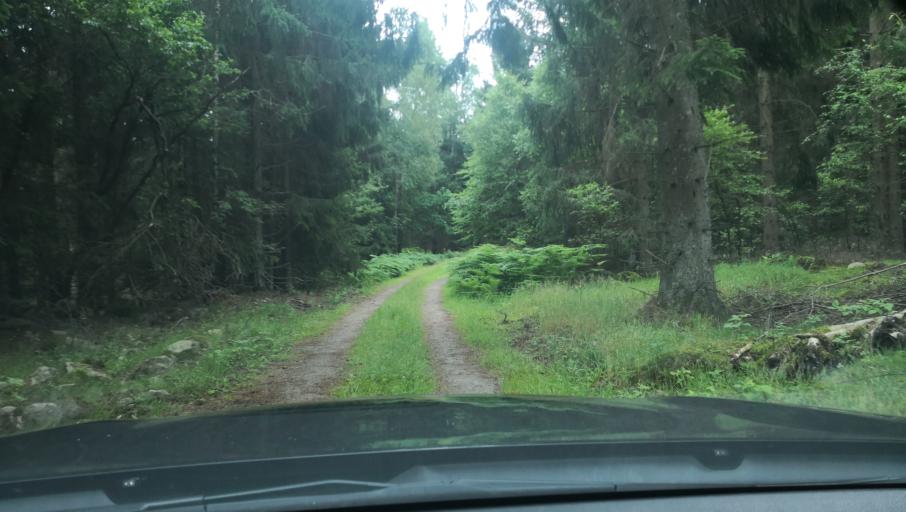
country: SE
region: Skane
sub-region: Simrishamns Kommun
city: Kivik
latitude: 55.6122
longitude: 14.1194
